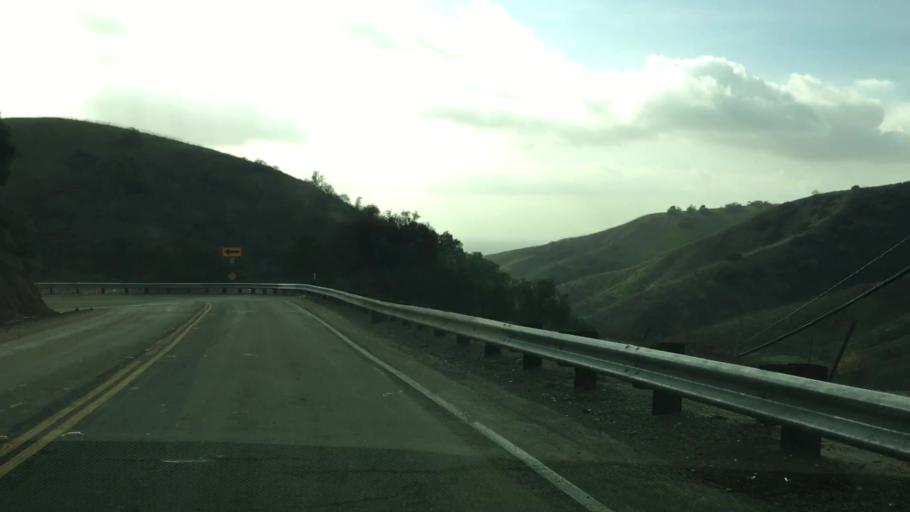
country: US
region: California
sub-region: Los Angeles County
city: Whittier
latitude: 33.9949
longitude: -118.0130
